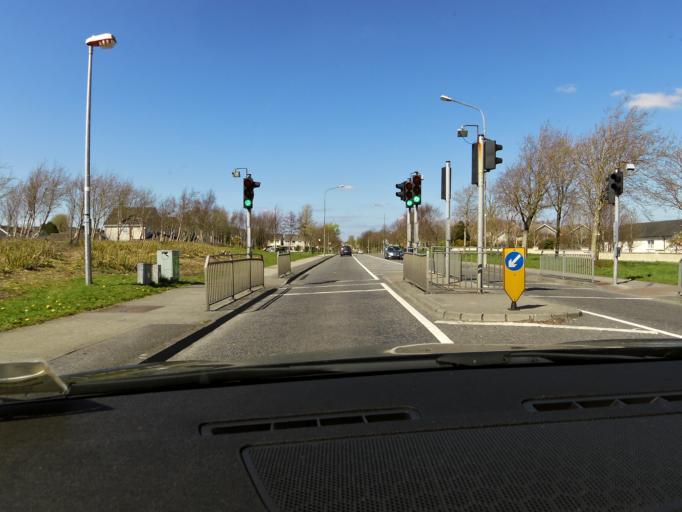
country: IE
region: Connaught
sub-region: County Galway
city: Gaillimh
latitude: 53.2829
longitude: -9.0723
